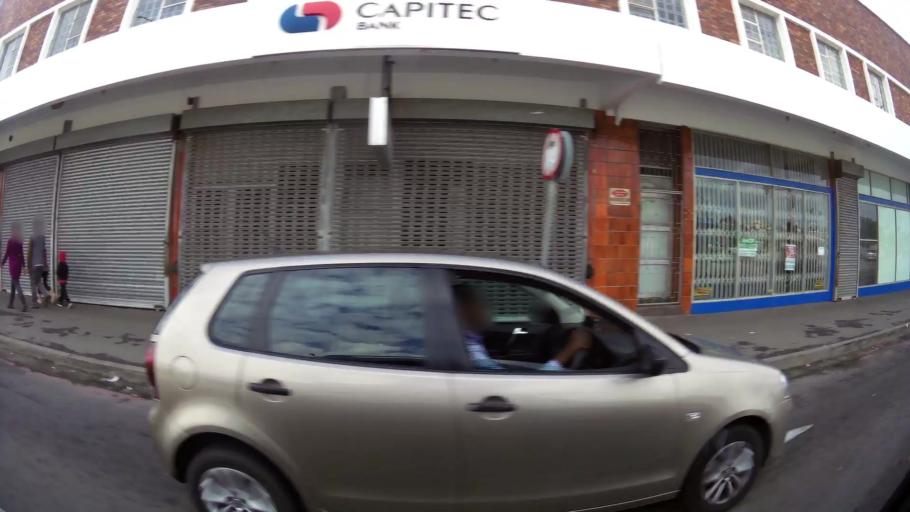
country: ZA
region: Eastern Cape
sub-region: Nelson Mandela Bay Metropolitan Municipality
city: Port Elizabeth
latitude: -33.9346
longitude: 25.5847
